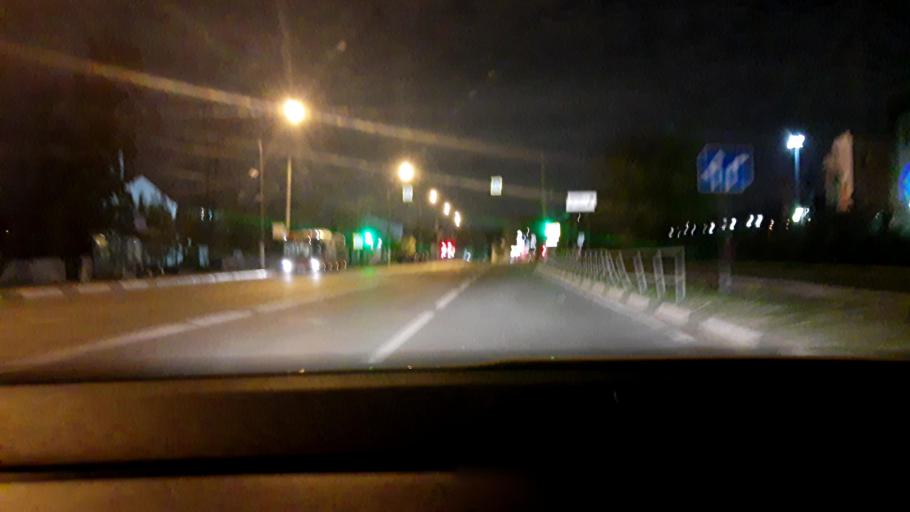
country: RU
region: Moskovskaya
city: Dolgoprudnyy
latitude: 55.9359
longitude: 37.5120
